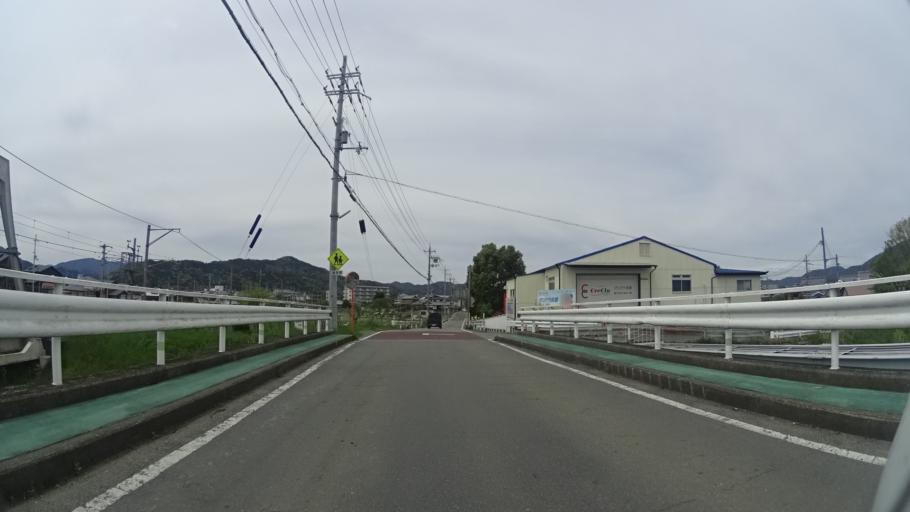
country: JP
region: Kyoto
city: Kameoka
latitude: 35.0263
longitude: 135.5616
